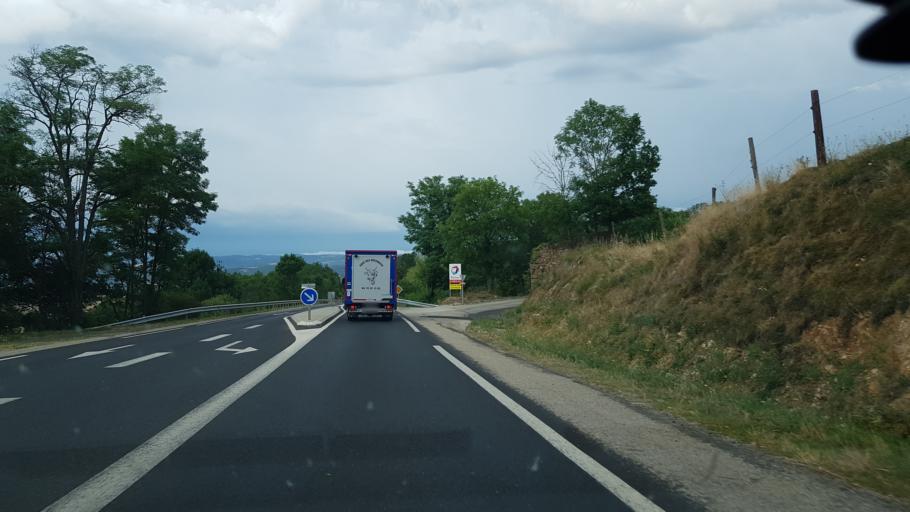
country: FR
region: Auvergne
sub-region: Departement de la Haute-Loire
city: Brioude
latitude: 45.2849
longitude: 3.3572
